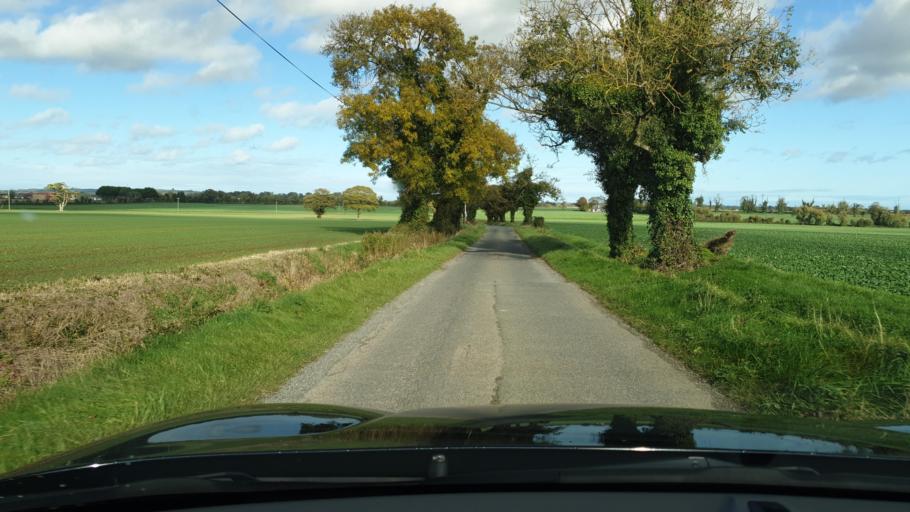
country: IE
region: Leinster
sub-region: Fingal County
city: Swords
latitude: 53.4967
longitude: -6.2437
